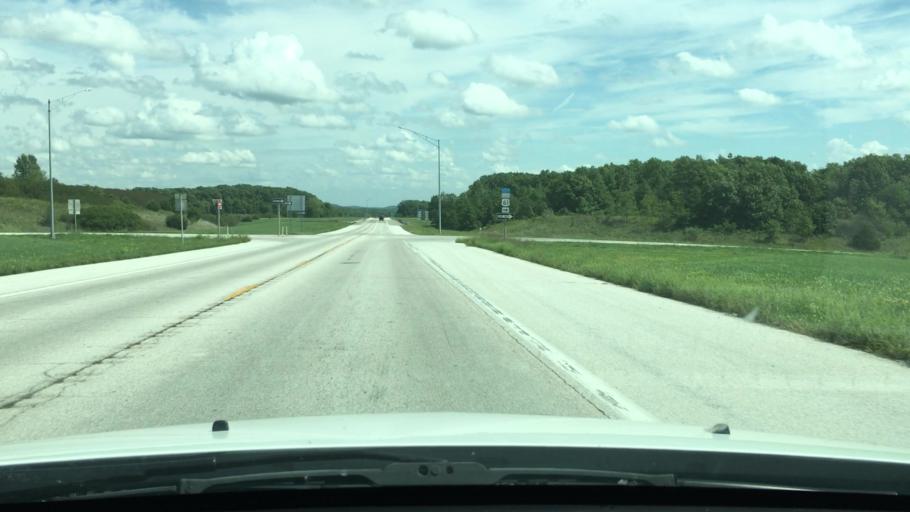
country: US
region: Missouri
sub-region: Pike County
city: Bowling Green
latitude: 39.3581
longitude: -91.2072
